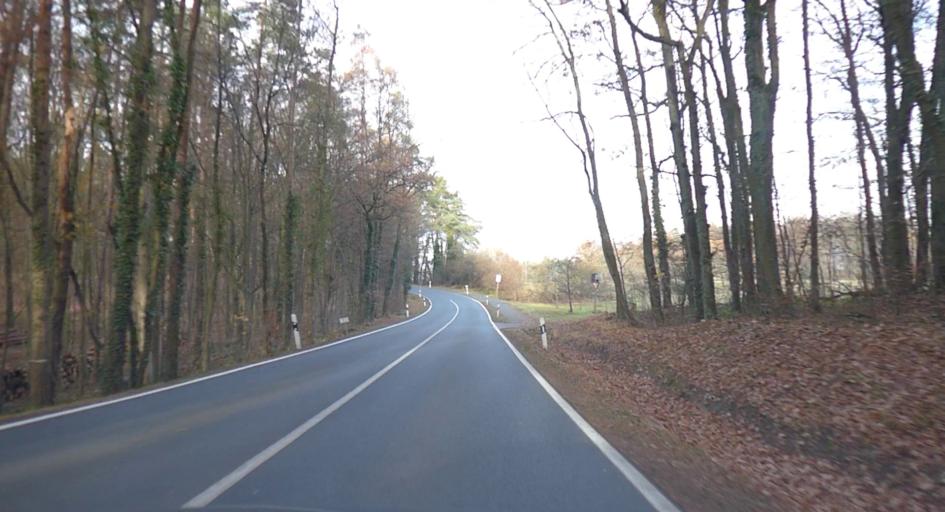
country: DE
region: Bavaria
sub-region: Regierungsbezirk Mittelfranken
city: Bubenreuth
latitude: 49.6265
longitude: 11.0390
